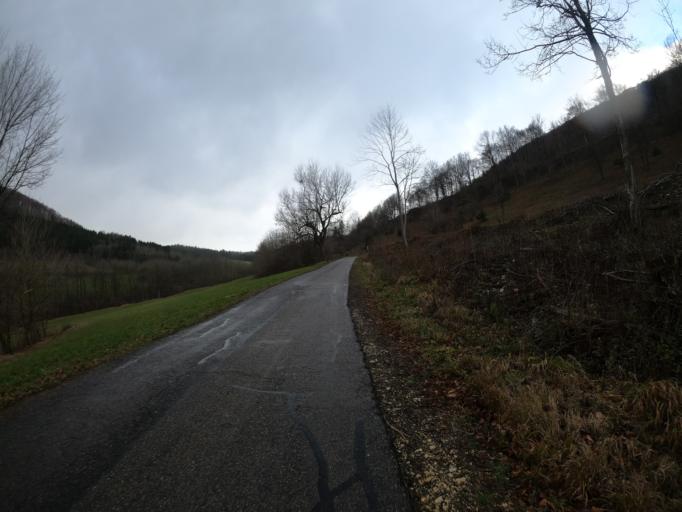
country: DE
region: Baden-Wuerttemberg
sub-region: Regierungsbezirk Stuttgart
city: Waldstetten
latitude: 48.7237
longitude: 9.8461
